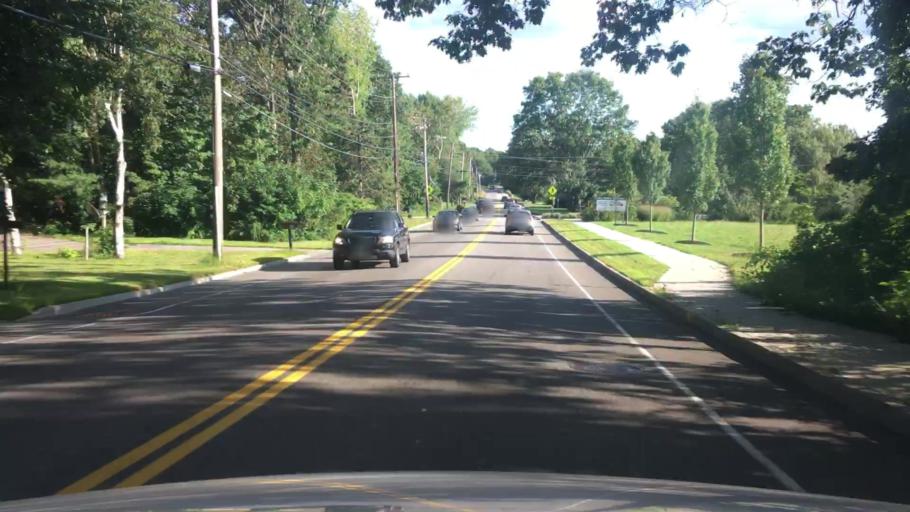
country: US
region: Maine
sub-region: Cumberland County
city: Scarborough
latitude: 43.5859
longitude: -70.3335
